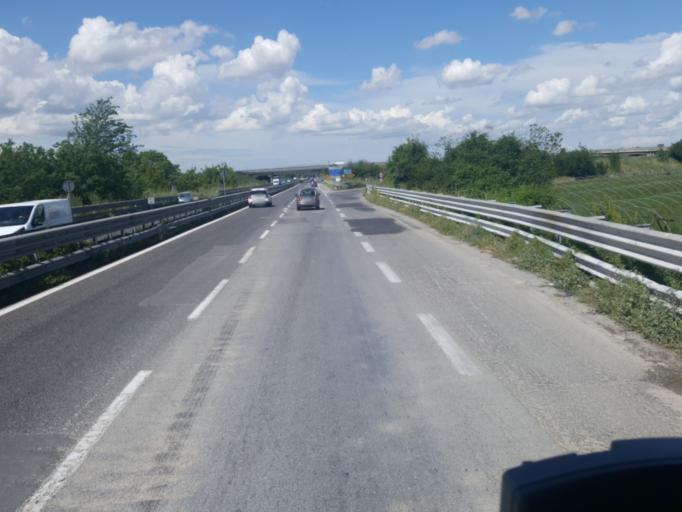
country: IT
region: Campania
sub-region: Provincia di Napoli
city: Pascarola
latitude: 40.9735
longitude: 14.2978
